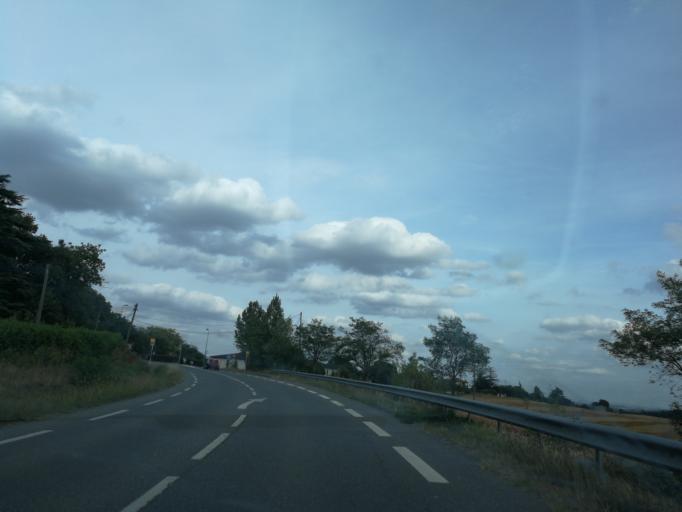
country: FR
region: Midi-Pyrenees
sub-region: Departement de la Haute-Garonne
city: Balma
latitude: 43.6112
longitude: 1.5305
